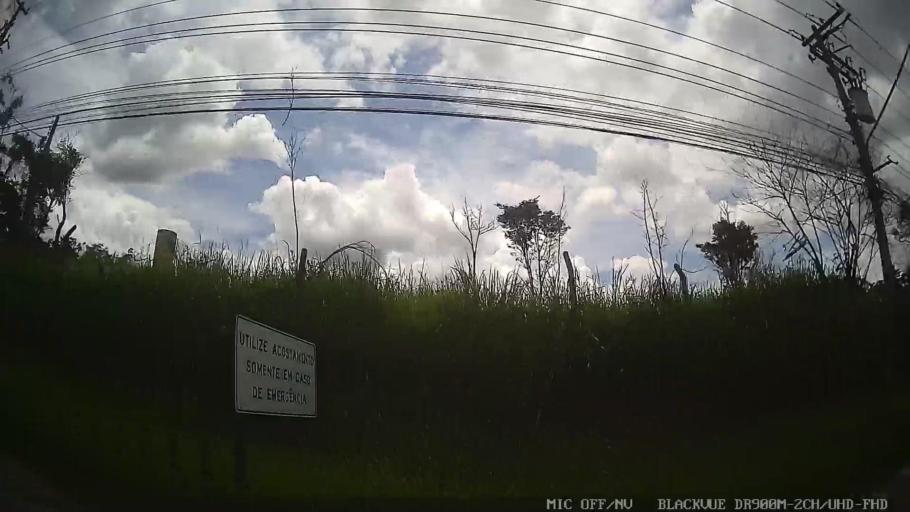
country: BR
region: Sao Paulo
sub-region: Suzano
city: Suzano
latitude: -23.5791
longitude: -46.3056
